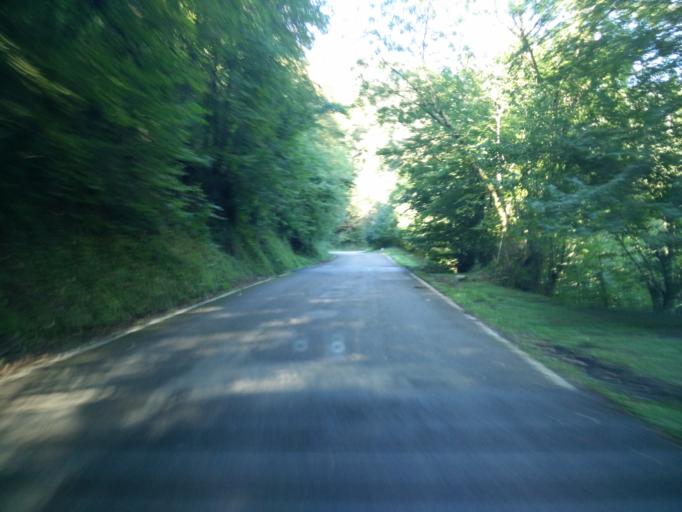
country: ES
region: Cantabria
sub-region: Provincia de Cantabria
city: Ruente
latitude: 43.1214
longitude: -4.2940
